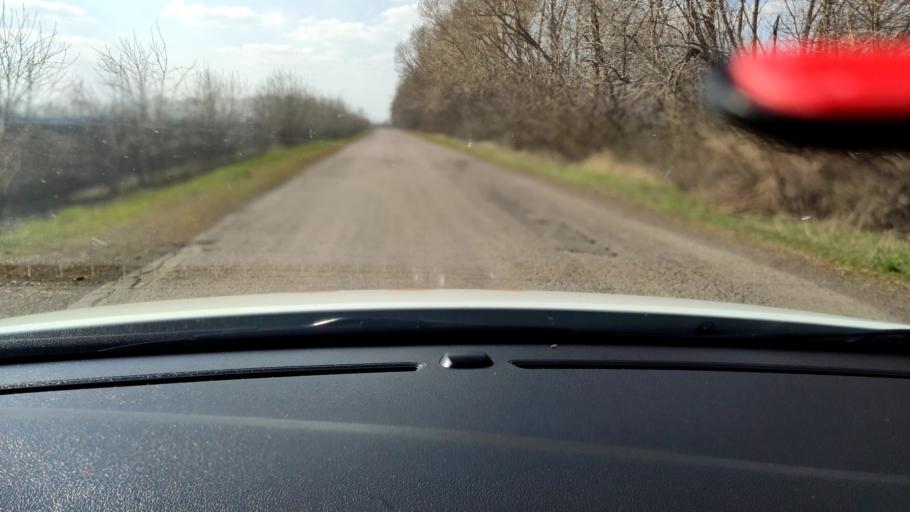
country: RU
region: Voronezj
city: Uryv-Pokrovka
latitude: 51.1289
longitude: 39.1064
